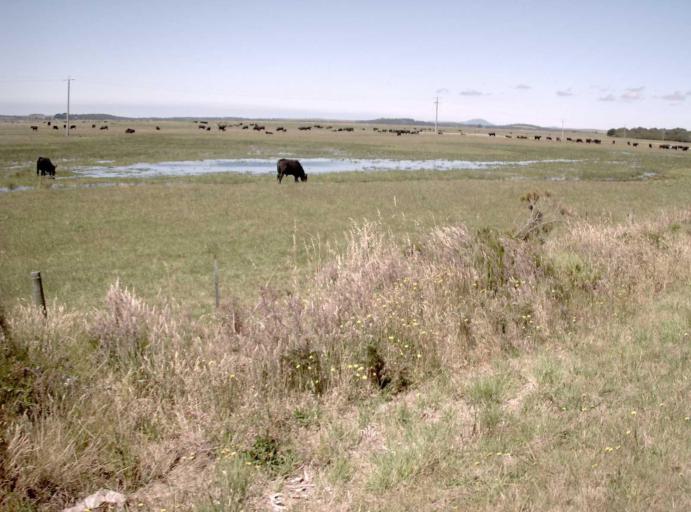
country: AU
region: Victoria
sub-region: Bass Coast
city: North Wonthaggi
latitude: -38.8159
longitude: 146.1068
